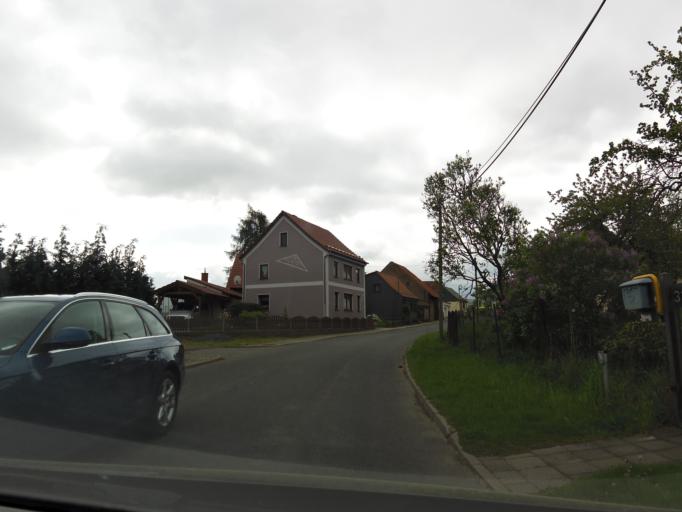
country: DE
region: Thuringia
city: Ernstroda
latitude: 50.8793
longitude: 10.6153
